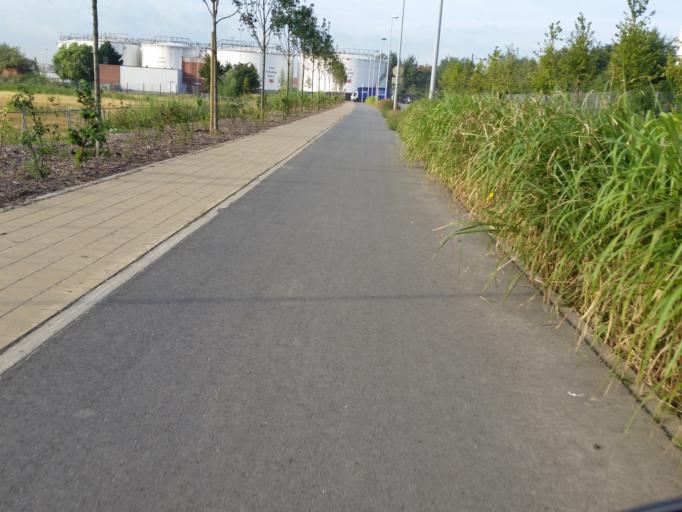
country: BE
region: Flanders
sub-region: Provincie Vlaams-Brabant
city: Diegem
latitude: 50.9071
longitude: 4.4057
